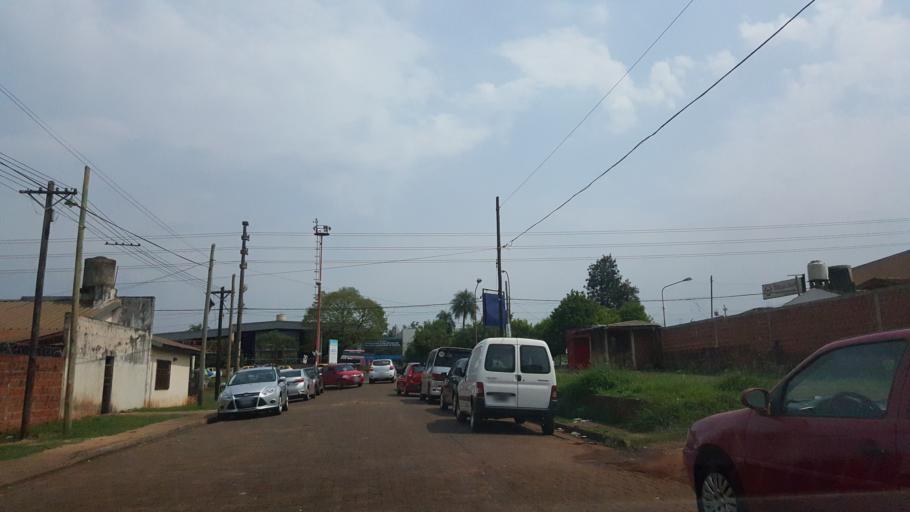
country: AR
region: Misiones
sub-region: Departamento de Capital
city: Posadas
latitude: -27.4016
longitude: -55.9131
